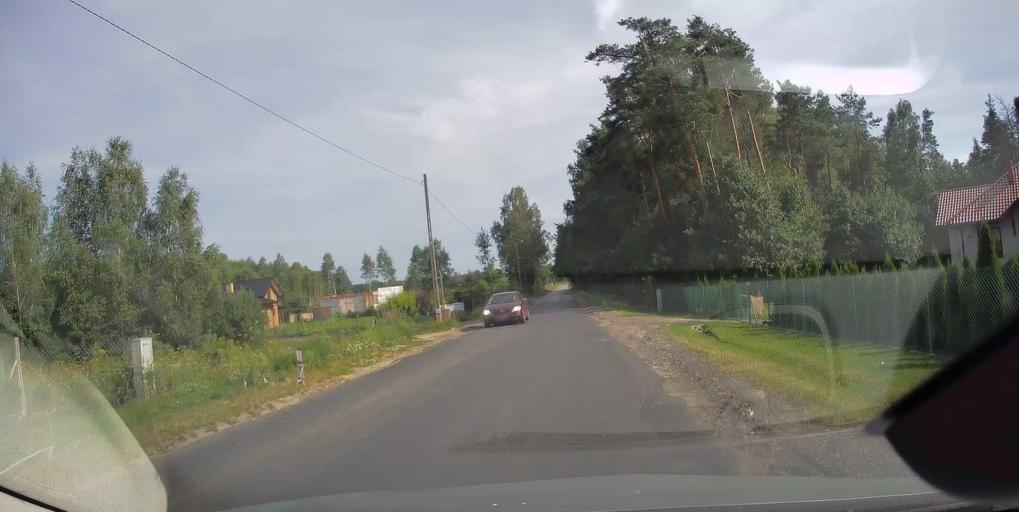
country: PL
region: Lodz Voivodeship
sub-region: Powiat tomaszowski
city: Tomaszow Mazowiecki
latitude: 51.4603
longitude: 20.0334
